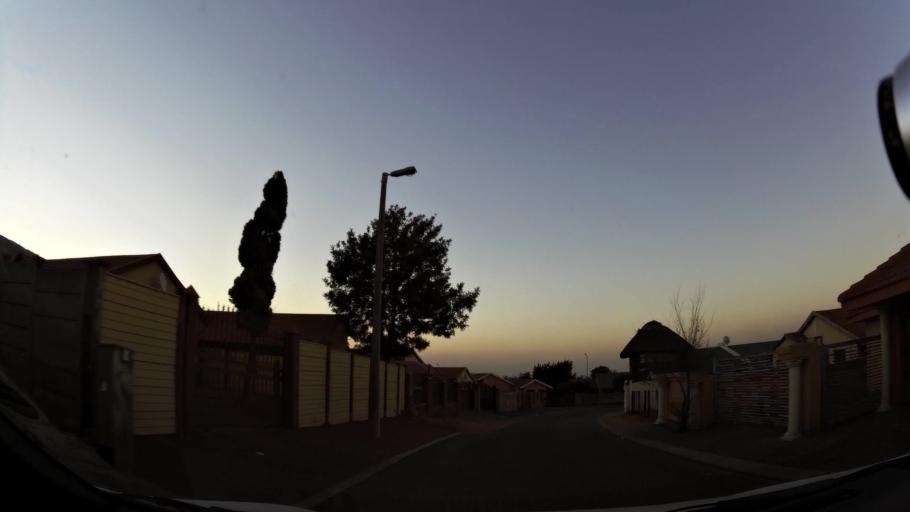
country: ZA
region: North-West
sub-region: Bojanala Platinum District Municipality
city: Rustenburg
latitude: -25.6519
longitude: 27.2023
